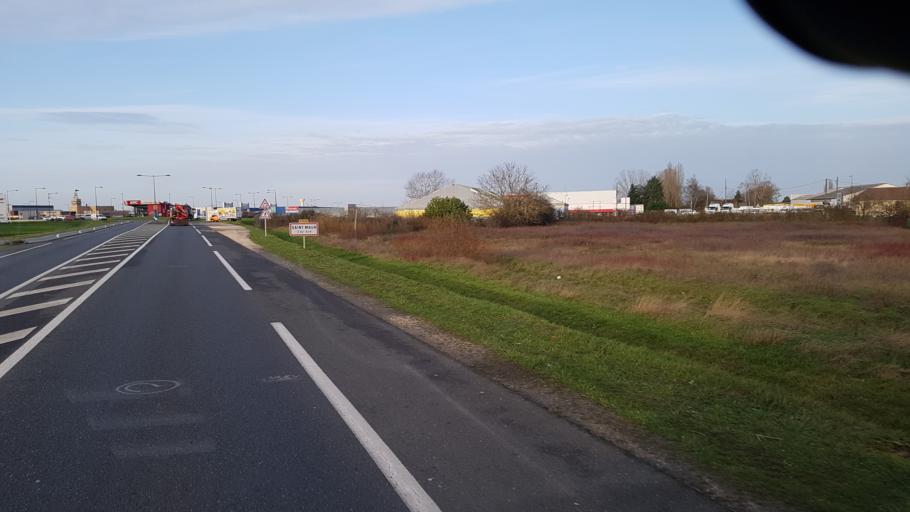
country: FR
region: Centre
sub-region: Departement de l'Indre
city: Saint-Maur
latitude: 46.7889
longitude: 1.6634
